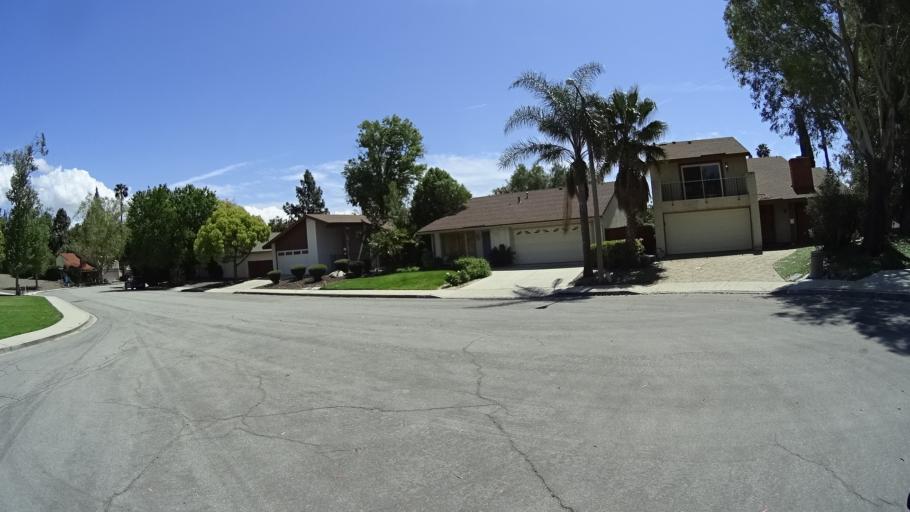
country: US
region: California
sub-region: Ventura County
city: Thousand Oaks
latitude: 34.2154
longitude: -118.8439
